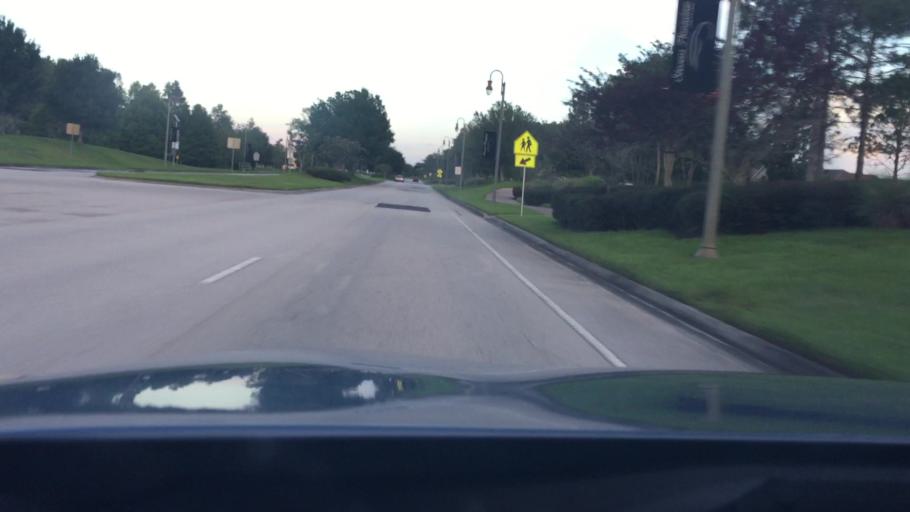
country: US
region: Florida
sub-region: Osceola County
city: Saint Cloud
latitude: 28.2273
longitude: -81.3020
